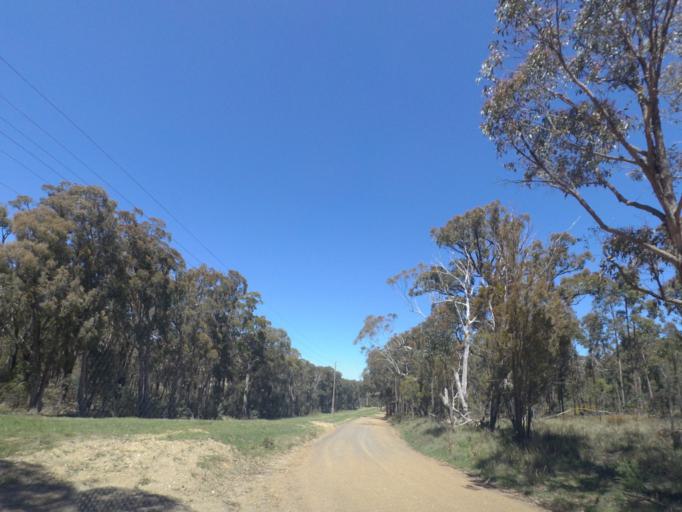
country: AU
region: Victoria
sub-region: Hume
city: Sunbury
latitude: -37.4033
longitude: 144.5619
